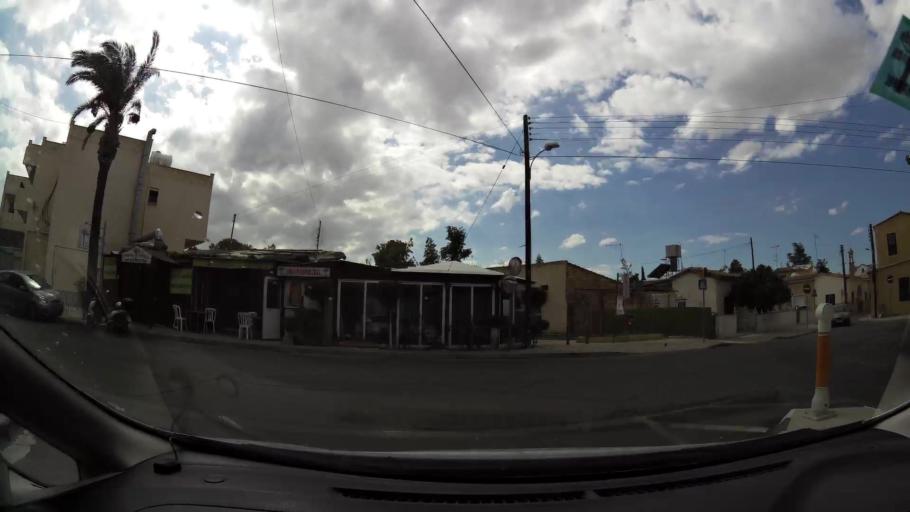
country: CY
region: Lefkosia
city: Nicosia
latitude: 35.1738
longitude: 33.3810
